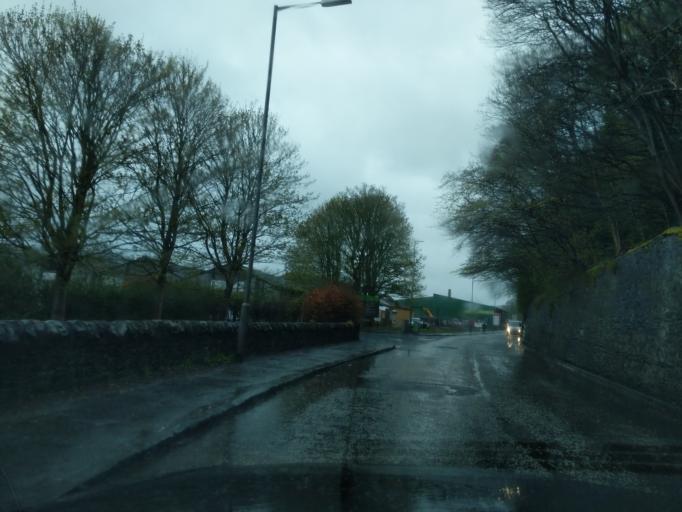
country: GB
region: Scotland
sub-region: The Scottish Borders
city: Selkirk
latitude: 55.5510
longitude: -2.8449
